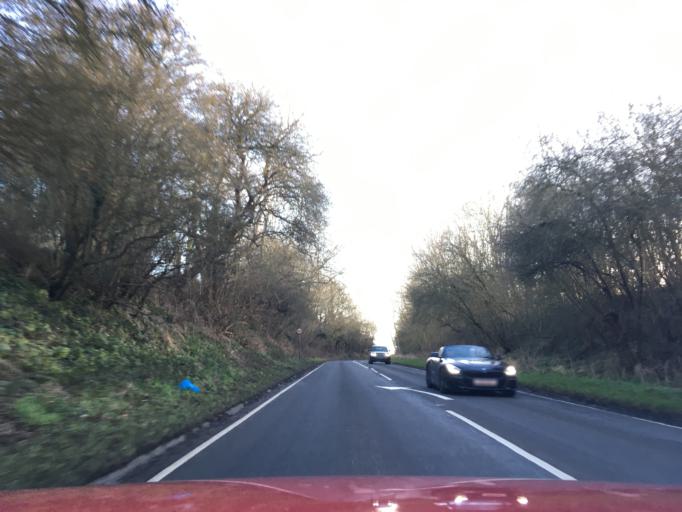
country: GB
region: England
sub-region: Warwickshire
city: Henley in Arden
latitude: 52.2630
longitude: -1.7672
